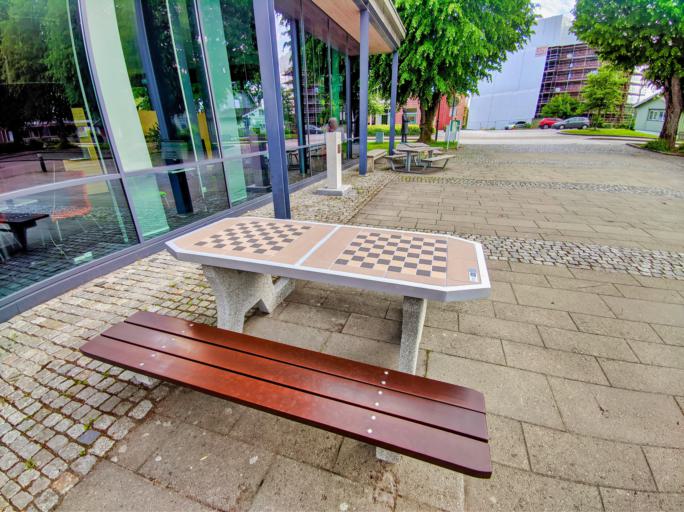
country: NO
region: Ostfold
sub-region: Eidsberg
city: Mysen
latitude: 59.5529
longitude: 11.3307
